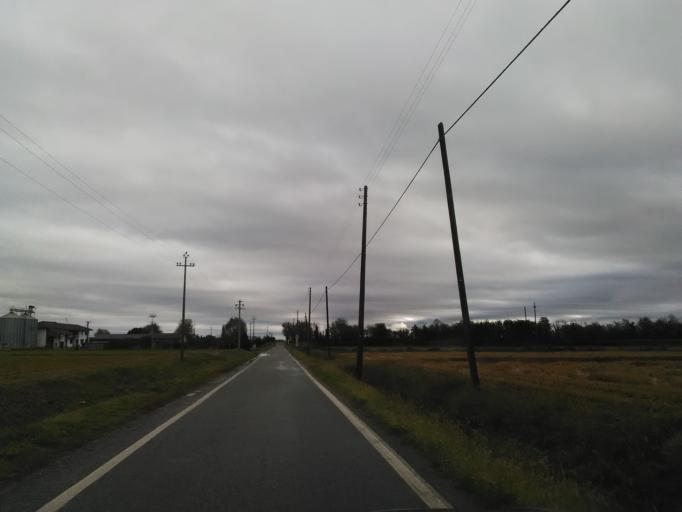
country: IT
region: Piedmont
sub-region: Provincia di Vercelli
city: Carisio
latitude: 45.4055
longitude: 8.2100
